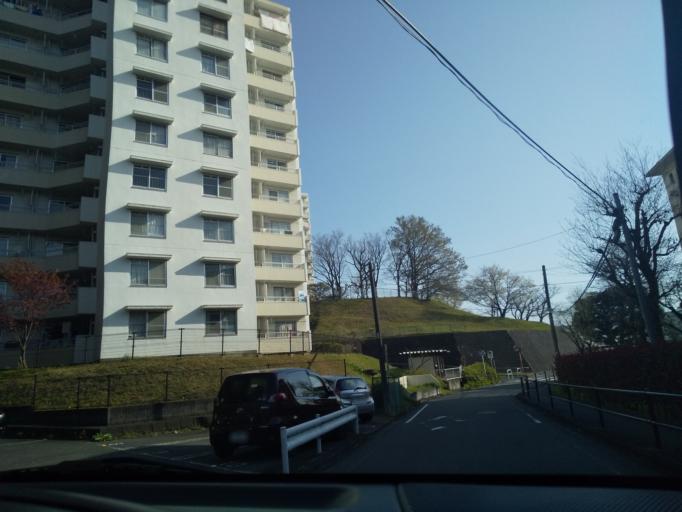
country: JP
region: Tokyo
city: Hino
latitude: 35.6481
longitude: 139.4174
